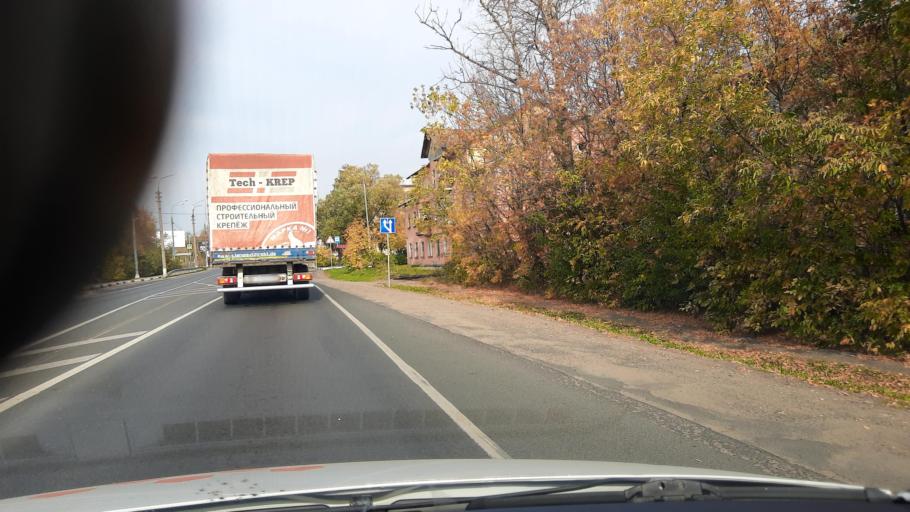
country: RU
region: Moskovskaya
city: Elektrostal'
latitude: 55.7881
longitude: 38.4312
